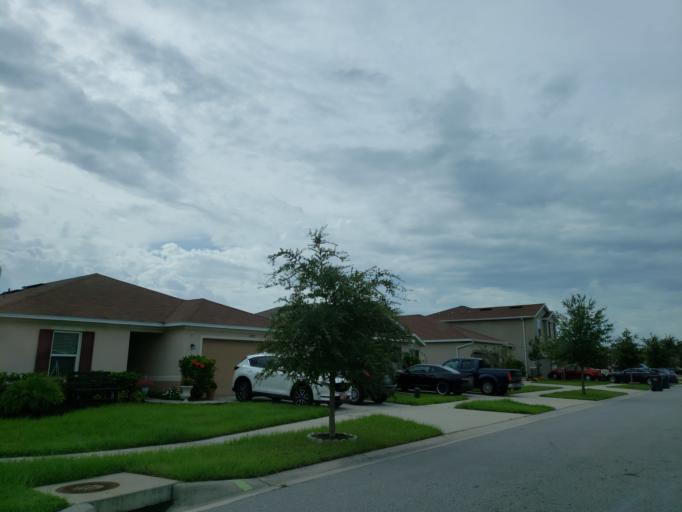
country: US
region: Florida
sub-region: Hillsborough County
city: Gibsonton
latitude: 27.8320
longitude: -82.3733
